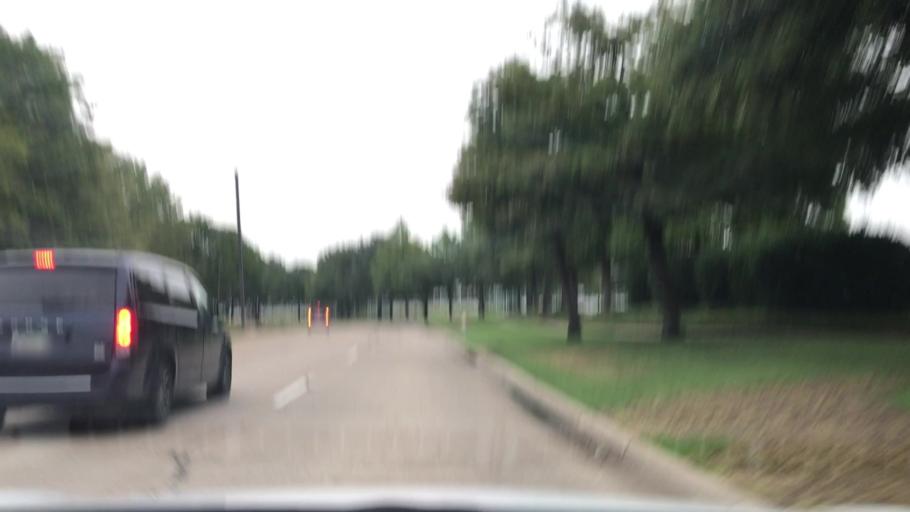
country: US
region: Texas
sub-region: Dallas County
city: Coppell
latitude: 32.9296
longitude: -97.0118
